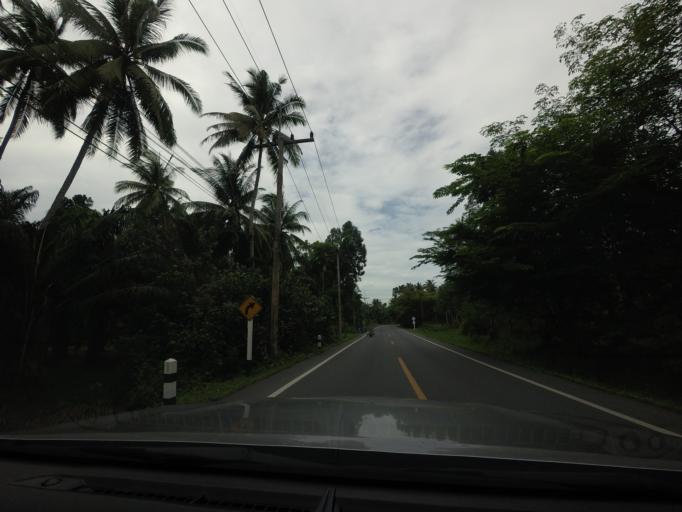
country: TH
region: Nakhon Si Thammarat
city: Phra Phrom
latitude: 8.2907
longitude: 99.9462
